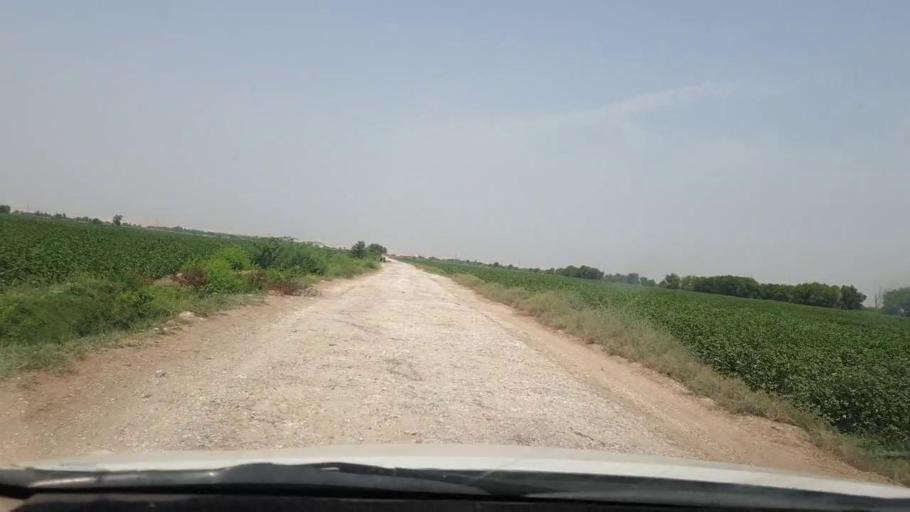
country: PK
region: Sindh
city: Rohri
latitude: 27.4977
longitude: 69.0181
